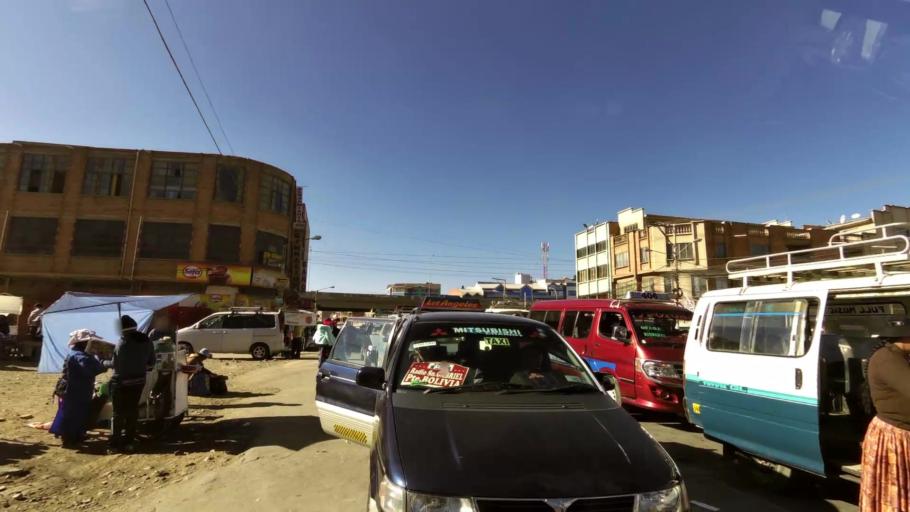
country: BO
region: La Paz
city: La Paz
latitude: -16.5338
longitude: -68.1913
